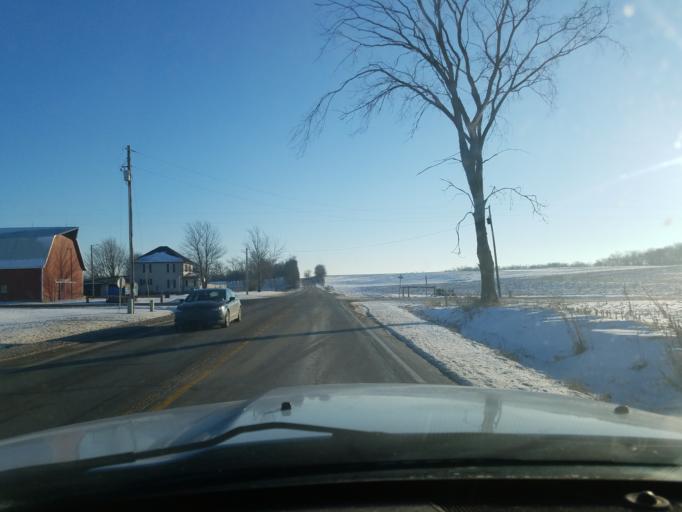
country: US
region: Indiana
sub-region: Noble County
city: Ligonier
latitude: 41.4554
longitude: -85.5392
